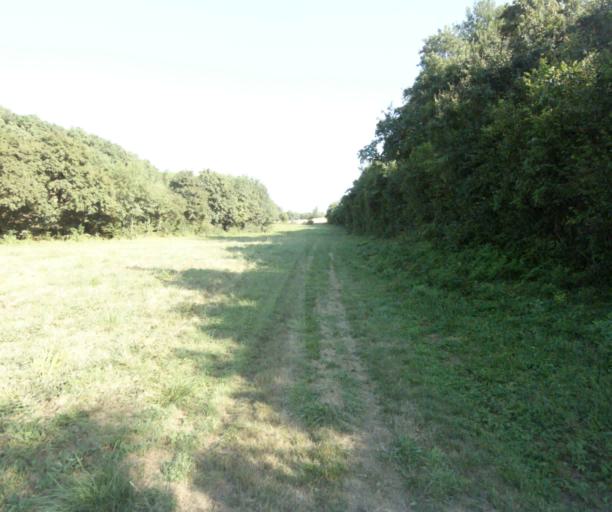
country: FR
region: Midi-Pyrenees
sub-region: Departement de la Haute-Garonne
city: Saint-Felix-Lauragais
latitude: 43.4344
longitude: 1.8234
